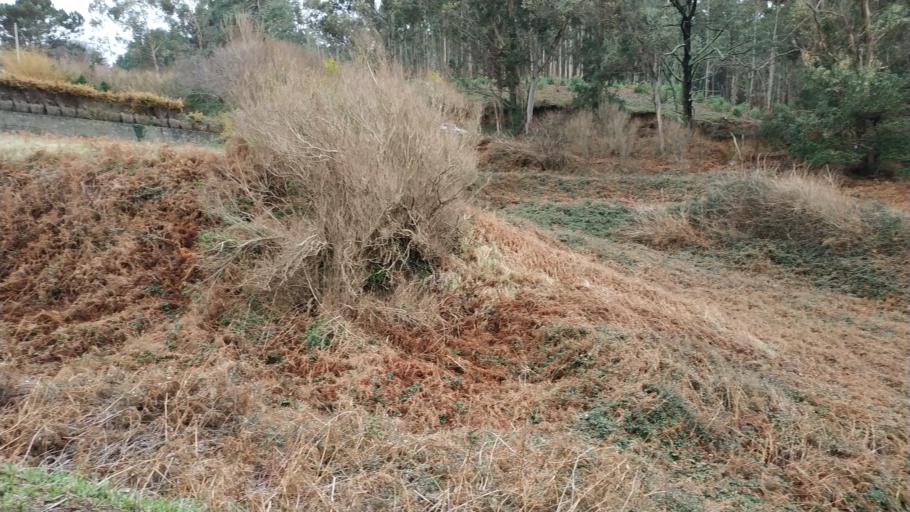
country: ES
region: Galicia
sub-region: Provincia da Coruna
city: Oleiros
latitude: 43.3990
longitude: -8.3293
